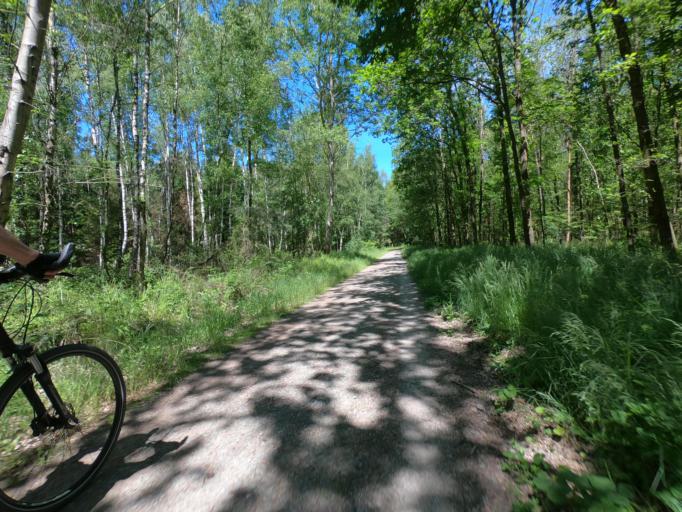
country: DE
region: Hesse
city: Heusenstamm
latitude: 50.0432
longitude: 8.7807
